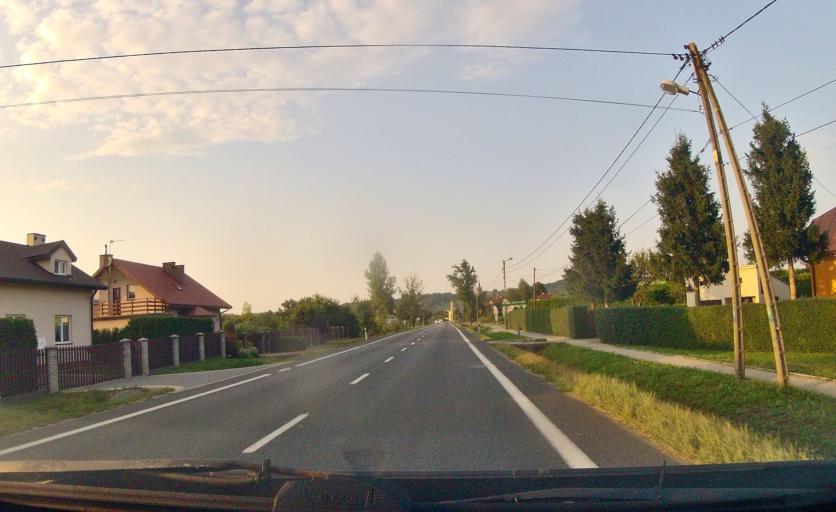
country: PL
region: Subcarpathian Voivodeship
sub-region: Powiat jasielski
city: Kolaczyce
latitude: 49.8004
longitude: 21.4313
